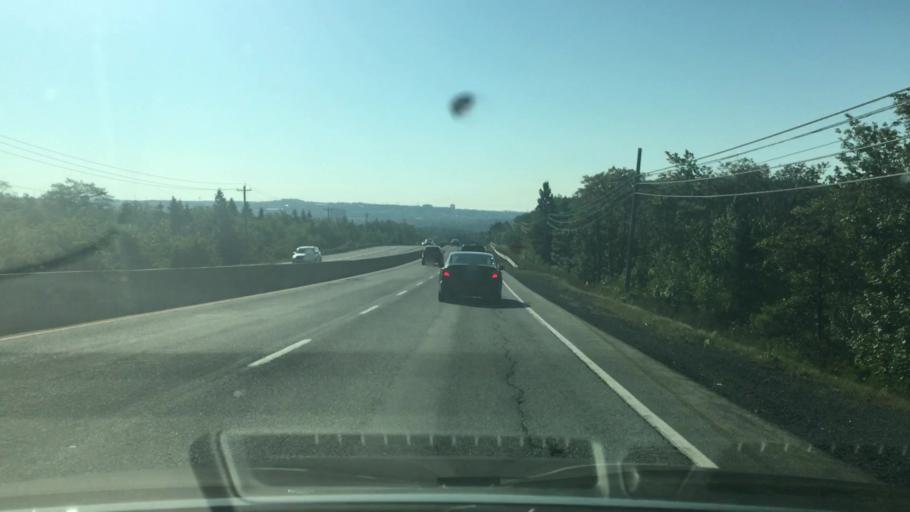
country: CA
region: Nova Scotia
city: Dartmouth
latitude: 44.7147
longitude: -63.6313
